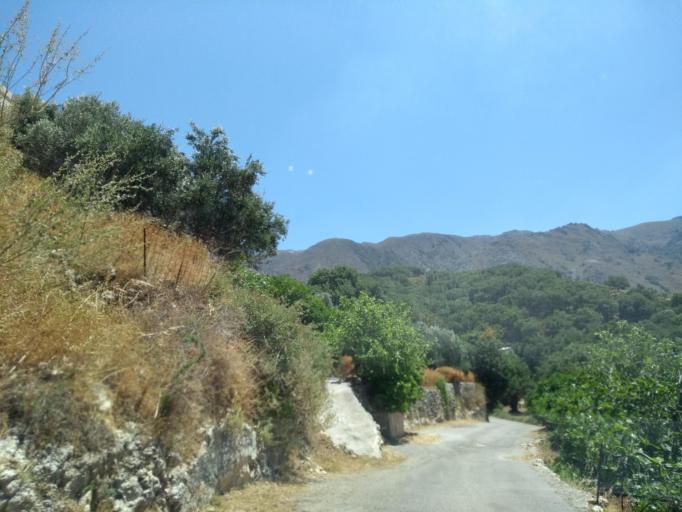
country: GR
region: Crete
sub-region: Nomos Chanias
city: Georgioupolis
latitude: 35.3120
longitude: 24.3092
